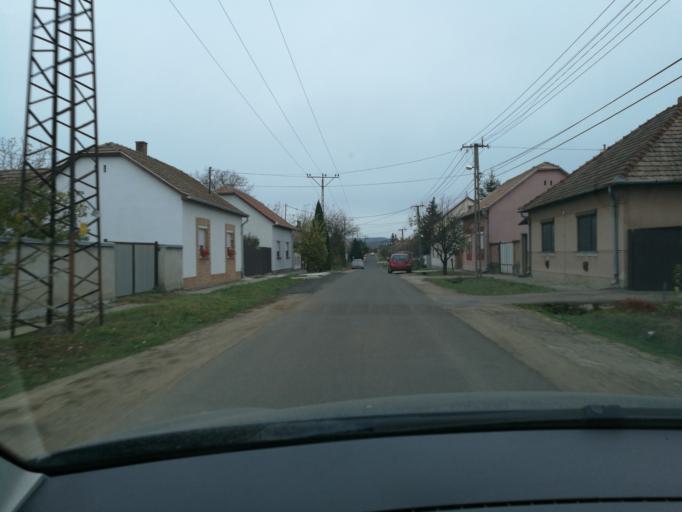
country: HU
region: Nograd
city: Szecseny
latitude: 48.0754
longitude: 19.5238
